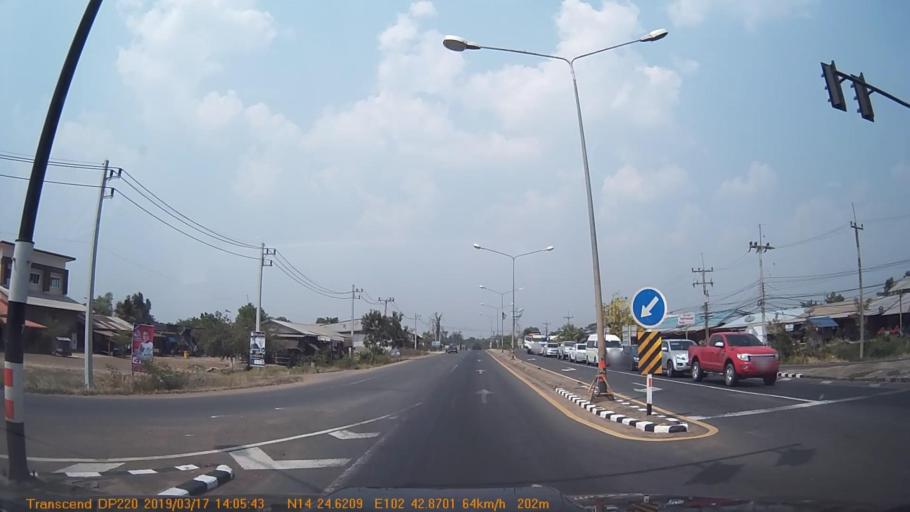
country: TH
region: Buriram
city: Pa Kham
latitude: 14.4107
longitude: 102.7146
